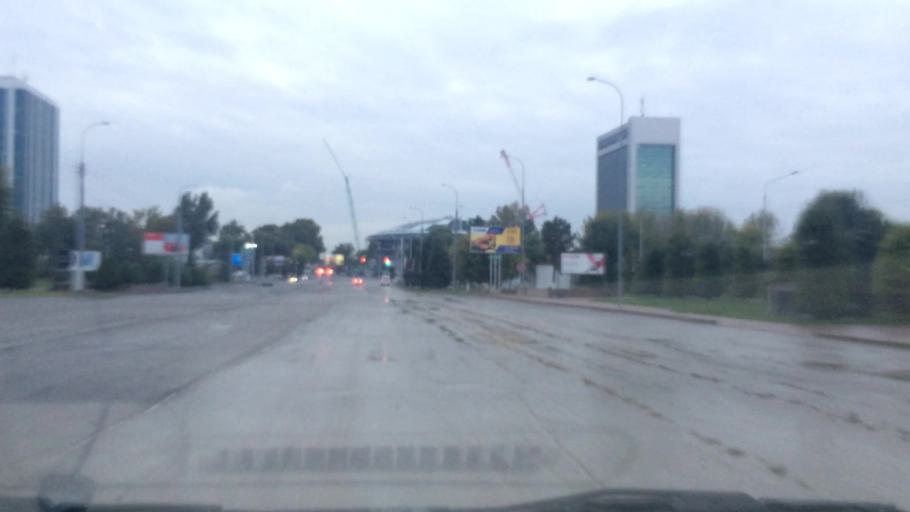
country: UZ
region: Toshkent Shahri
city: Tashkent
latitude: 41.3135
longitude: 69.2536
